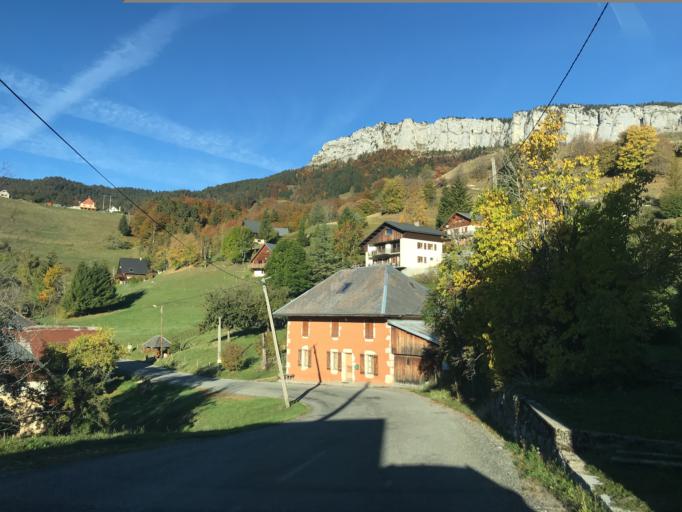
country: FR
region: Rhone-Alpes
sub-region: Departement de la Savoie
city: Vimines
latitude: 45.4608
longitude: 5.8651
